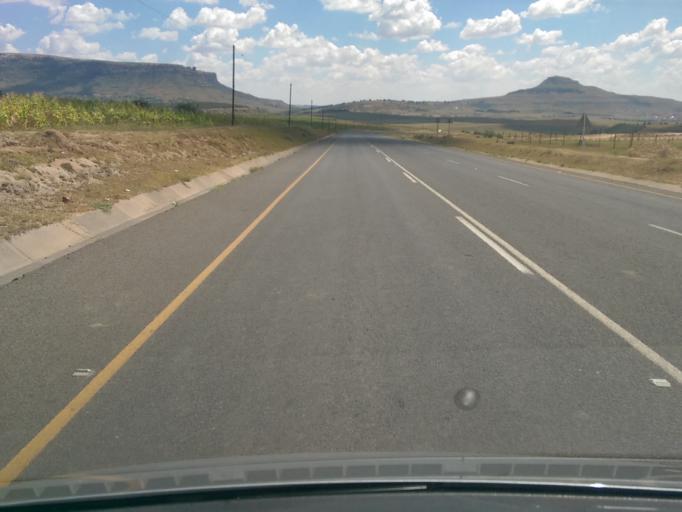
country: LS
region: Maseru
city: Maseru
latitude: -29.3966
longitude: 27.5171
